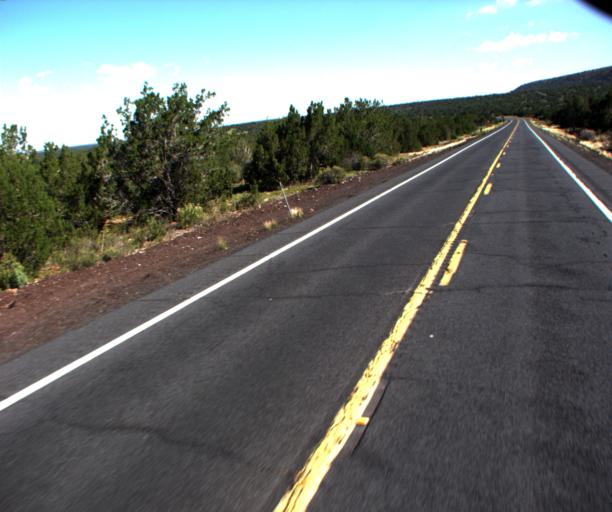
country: US
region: Arizona
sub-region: Coconino County
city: Williams
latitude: 35.4510
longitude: -112.1709
